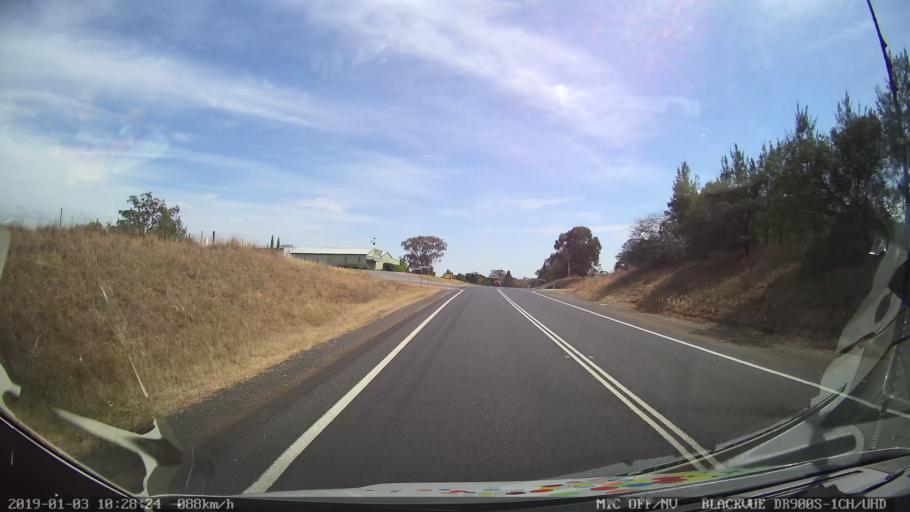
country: AU
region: New South Wales
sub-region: Young
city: Young
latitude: -34.3883
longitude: 148.2587
